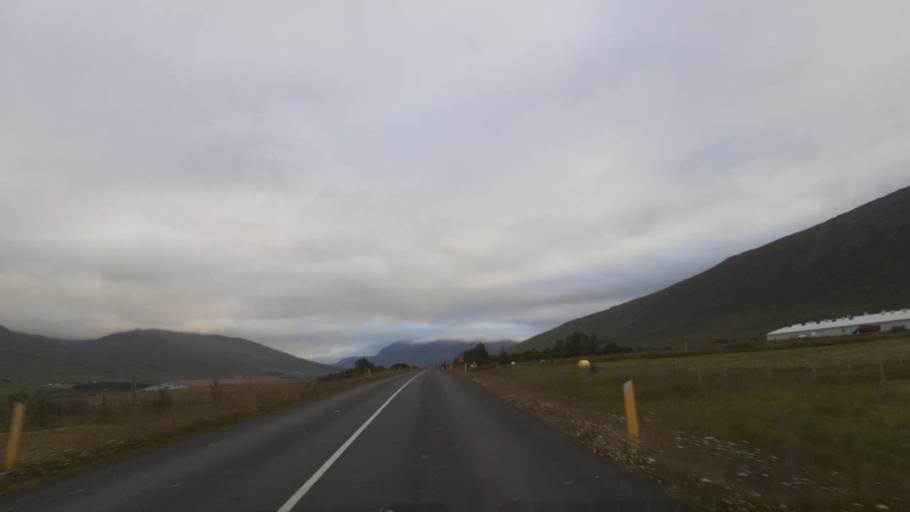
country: IS
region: Northeast
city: Dalvik
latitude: 65.9537
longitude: -18.5518
